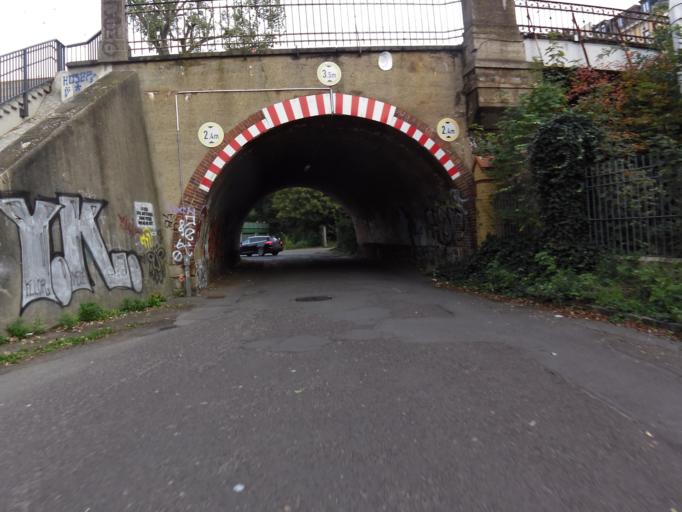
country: DE
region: Saxony
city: Leipzig
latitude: 51.3334
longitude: 12.4063
